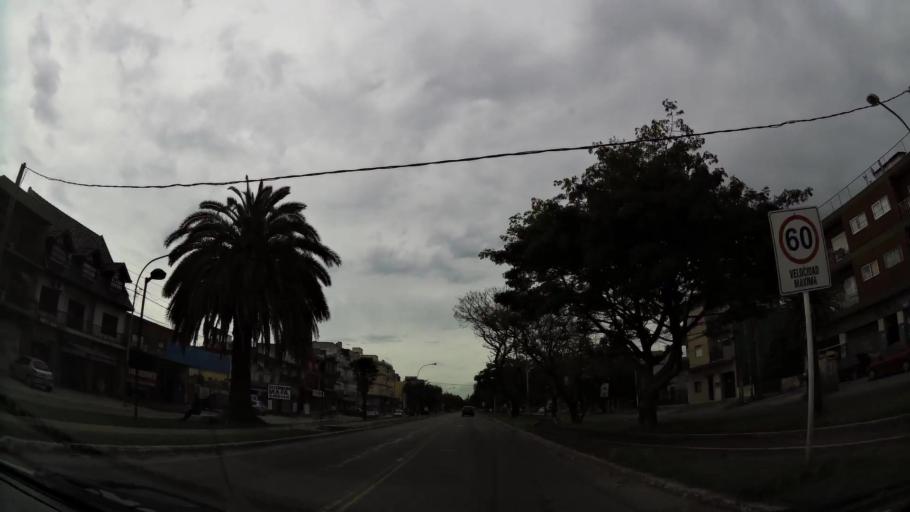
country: AR
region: Buenos Aires
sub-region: Partido de Quilmes
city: Quilmes
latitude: -34.7986
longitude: -58.2787
